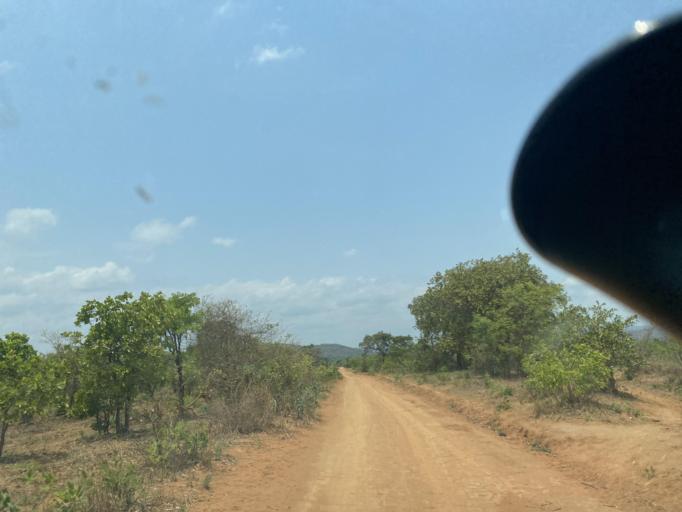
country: ZM
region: Lusaka
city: Chongwe
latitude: -15.5168
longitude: 28.8799
